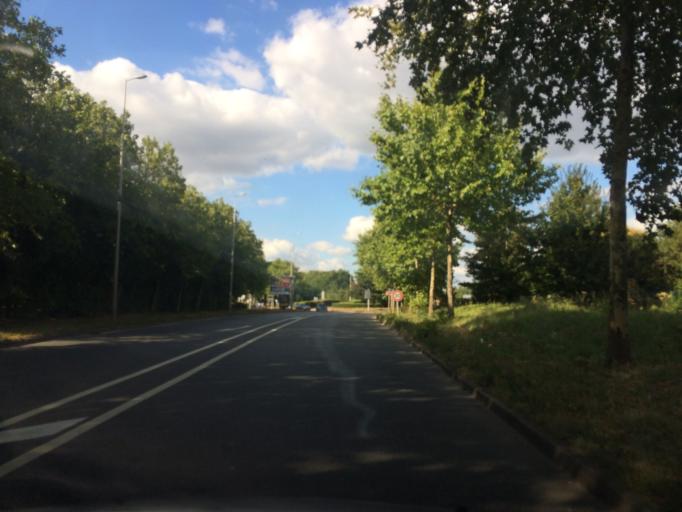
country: FR
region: Ile-de-France
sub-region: Departement de l'Essonne
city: Bondoufle
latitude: 48.6173
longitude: 2.3913
